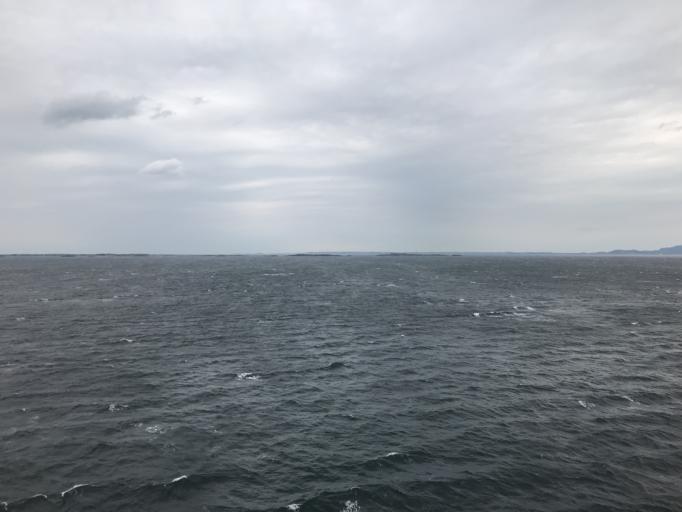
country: NO
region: Rogaland
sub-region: Randaberg
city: Randaberg
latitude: 59.0507
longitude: 5.5603
